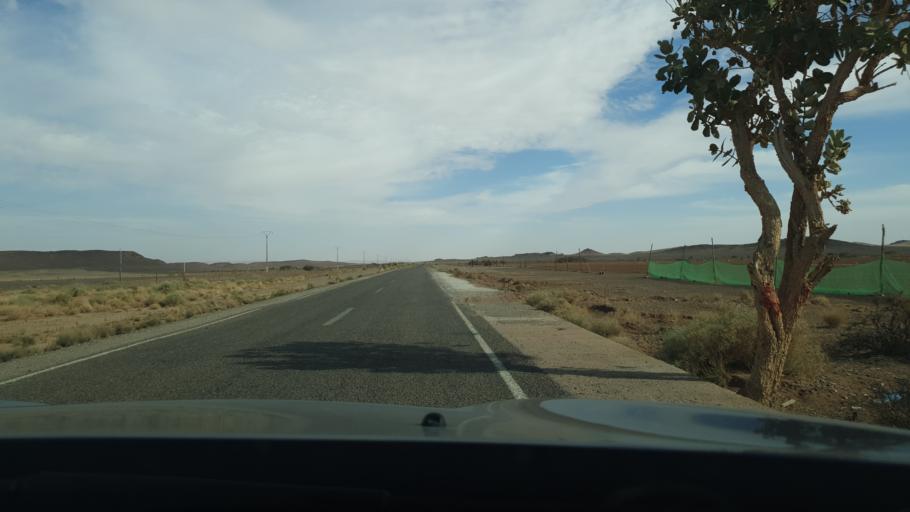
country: MA
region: Meknes-Tafilalet
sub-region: Errachidia
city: Goulmima
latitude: 31.5728
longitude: -4.8032
